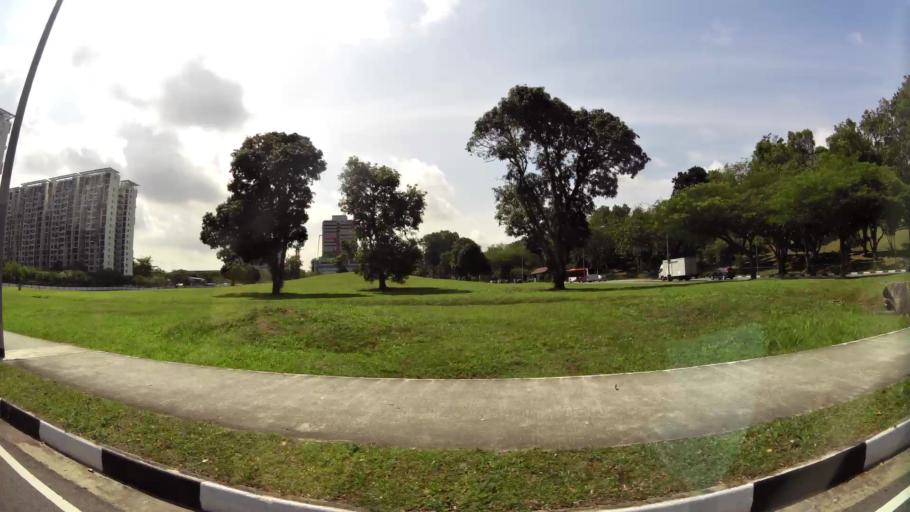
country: SG
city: Singapore
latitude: 1.3774
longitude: 103.8450
